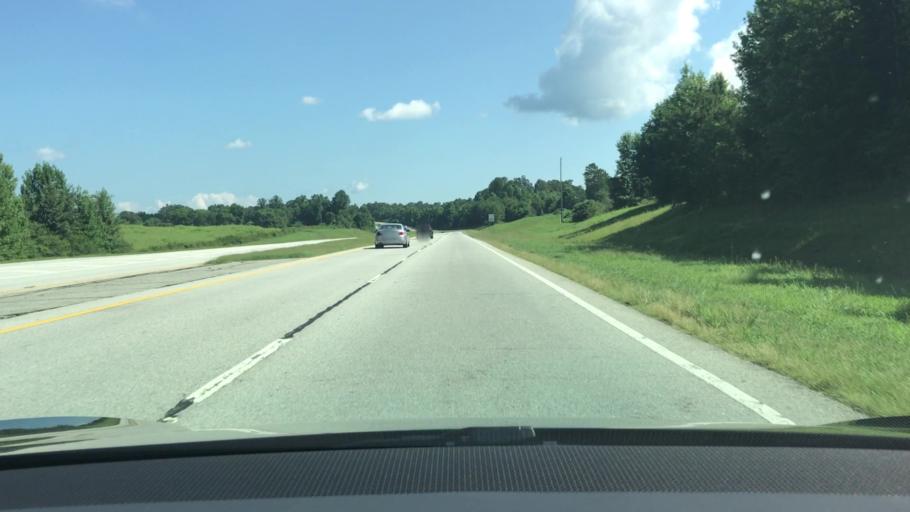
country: US
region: Georgia
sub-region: Habersham County
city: Clarkesville
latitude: 34.6156
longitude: -83.4482
